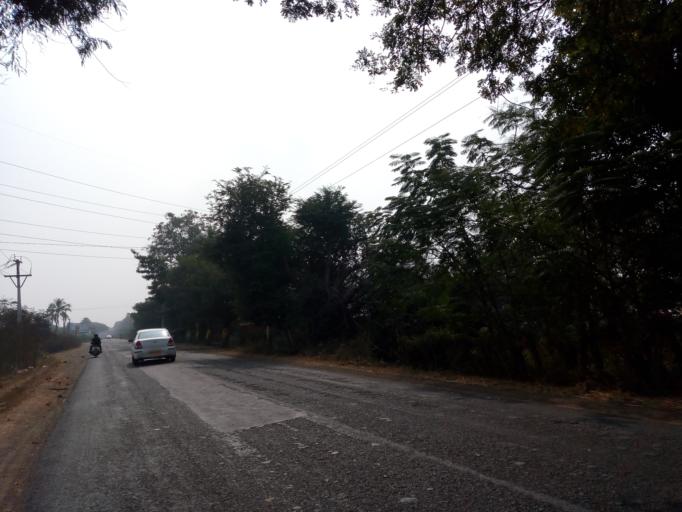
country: IN
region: Andhra Pradesh
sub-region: West Godavari
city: Bhimavaram
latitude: 16.5789
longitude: 81.4770
